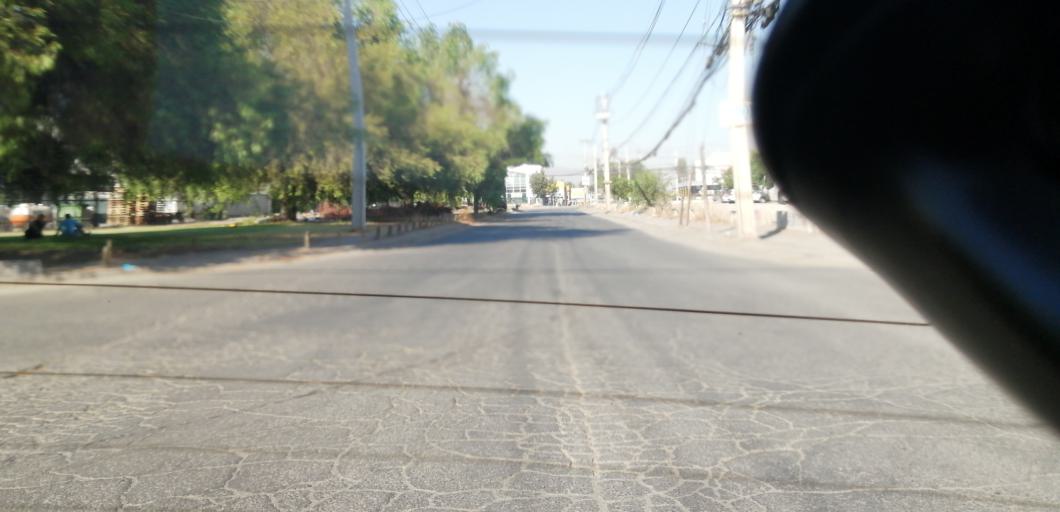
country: CL
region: Santiago Metropolitan
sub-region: Provincia de Santiago
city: Lo Prado
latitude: -33.3800
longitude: -70.7685
